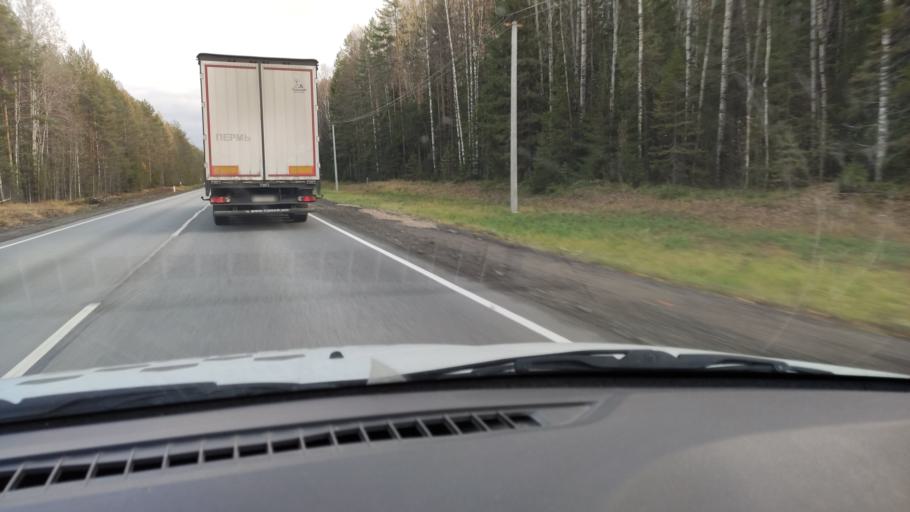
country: RU
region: Kirov
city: Dubrovka
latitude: 58.9107
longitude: 51.1733
